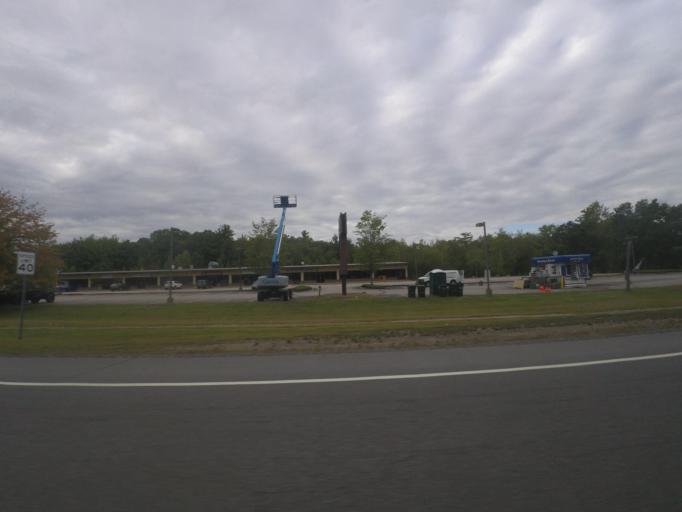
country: US
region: New Hampshire
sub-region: Strafford County
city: Rochester
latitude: 43.3212
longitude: -70.9536
